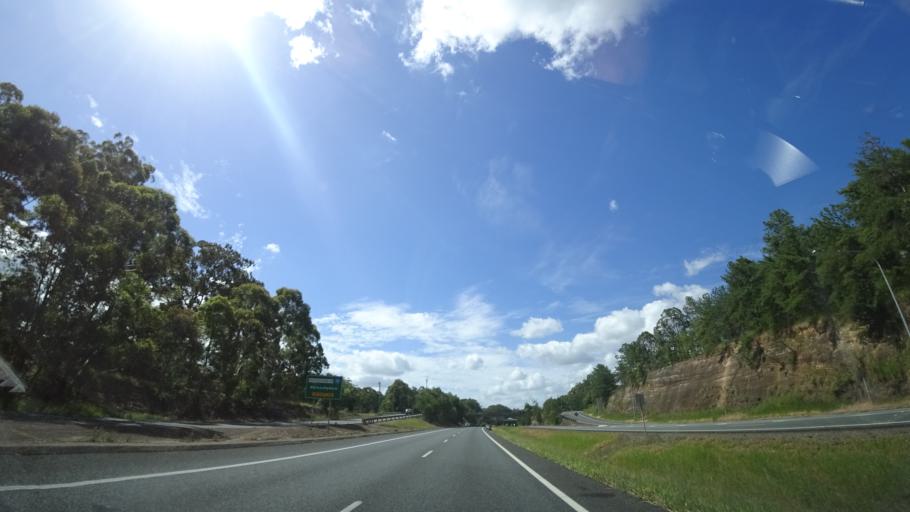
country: AU
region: Queensland
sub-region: Sunshine Coast
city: Woombye
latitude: -26.6764
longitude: 153.0001
